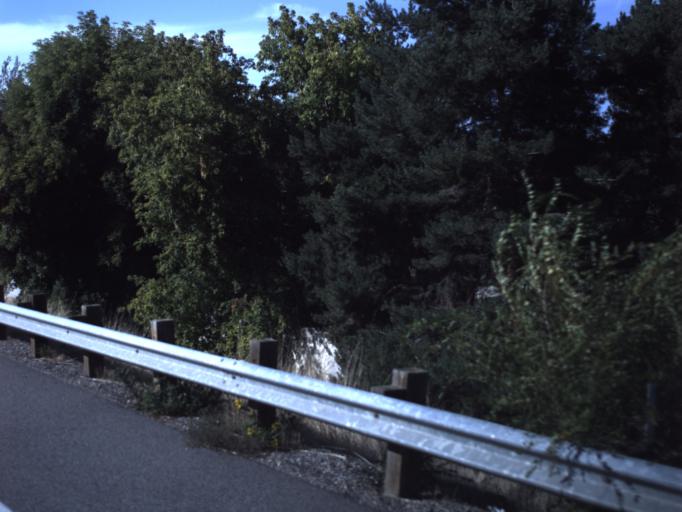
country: US
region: Utah
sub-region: Salt Lake County
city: Holladay
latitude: 40.6445
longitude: -111.8430
